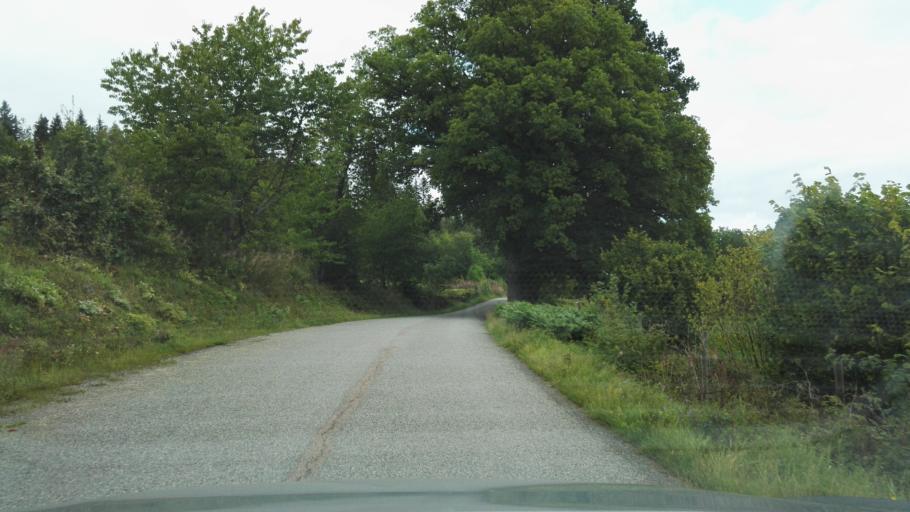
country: SE
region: Joenkoeping
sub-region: Vetlanda Kommun
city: Landsbro
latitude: 57.2327
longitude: 14.8309
